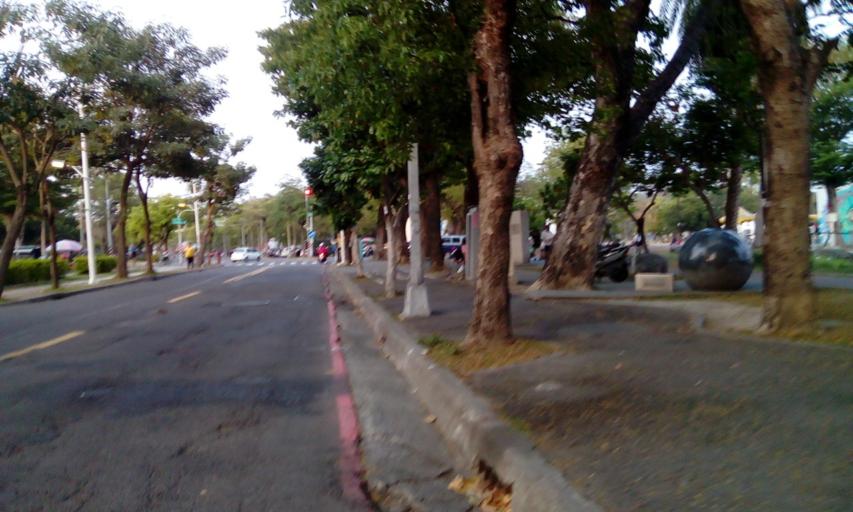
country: TW
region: Kaohsiung
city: Kaohsiung
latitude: 22.6873
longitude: 120.2972
